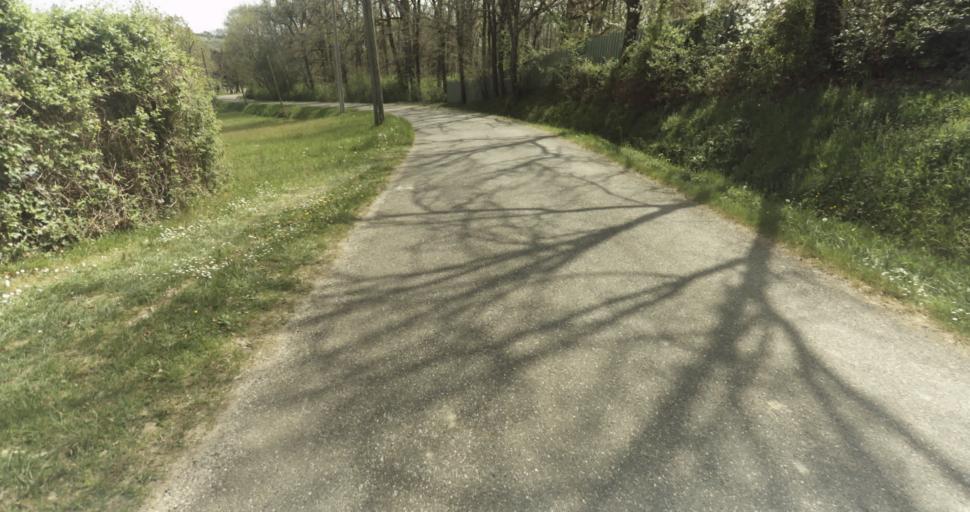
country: FR
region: Midi-Pyrenees
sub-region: Departement du Tarn-et-Garonne
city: Moissac
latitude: 44.1295
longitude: 1.0979
